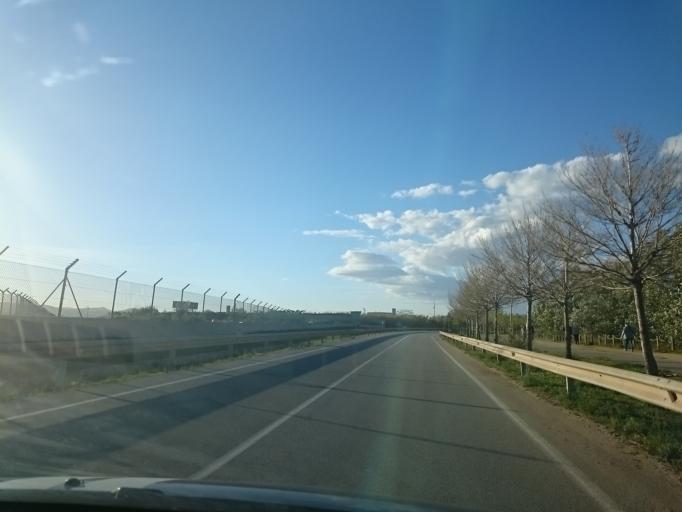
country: ES
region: Catalonia
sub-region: Provincia de Barcelona
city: El Prat de Llobregat
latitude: 41.3085
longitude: 2.1093
